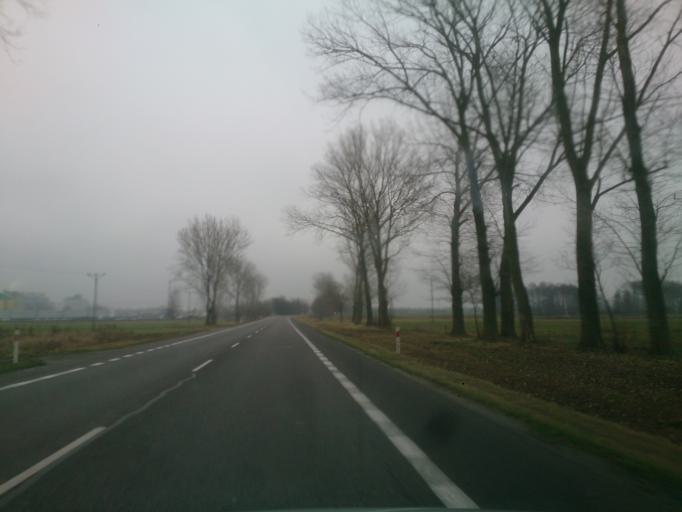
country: PL
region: Masovian Voivodeship
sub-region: Powiat plonski
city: Plonsk
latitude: 52.6161
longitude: 20.3402
